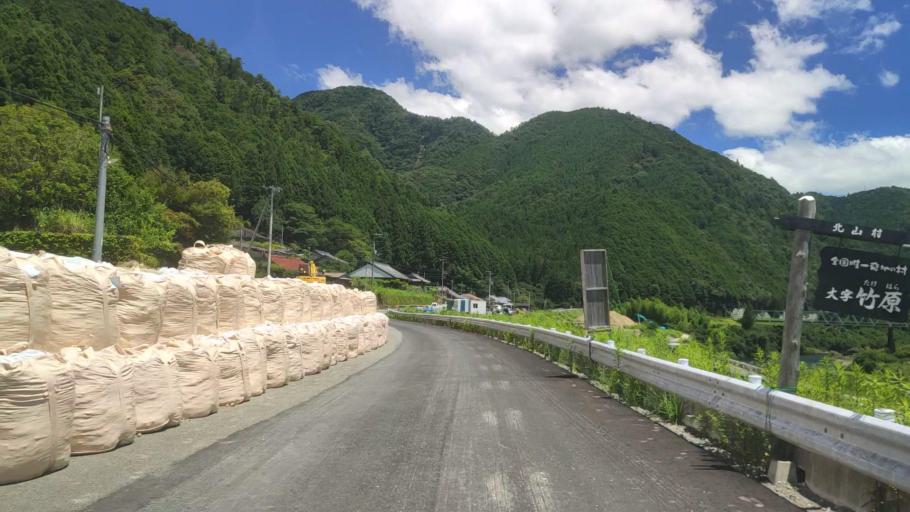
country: JP
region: Wakayama
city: Shingu
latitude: 33.9652
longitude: 135.9745
